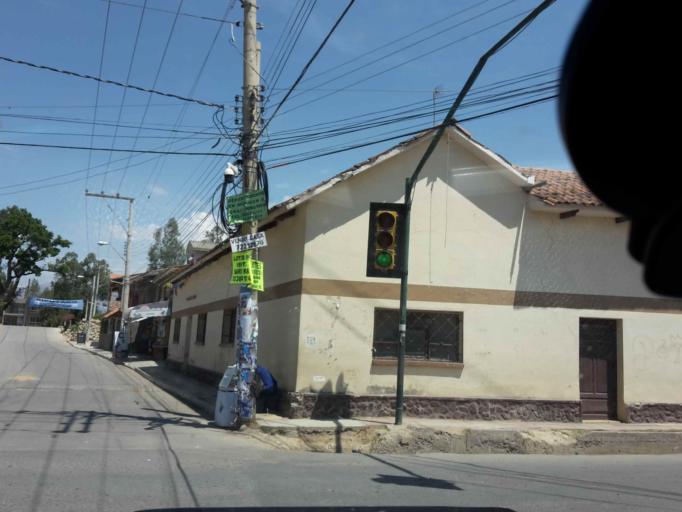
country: BO
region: Cochabamba
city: Cochabamba
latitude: -17.3607
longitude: -66.2288
